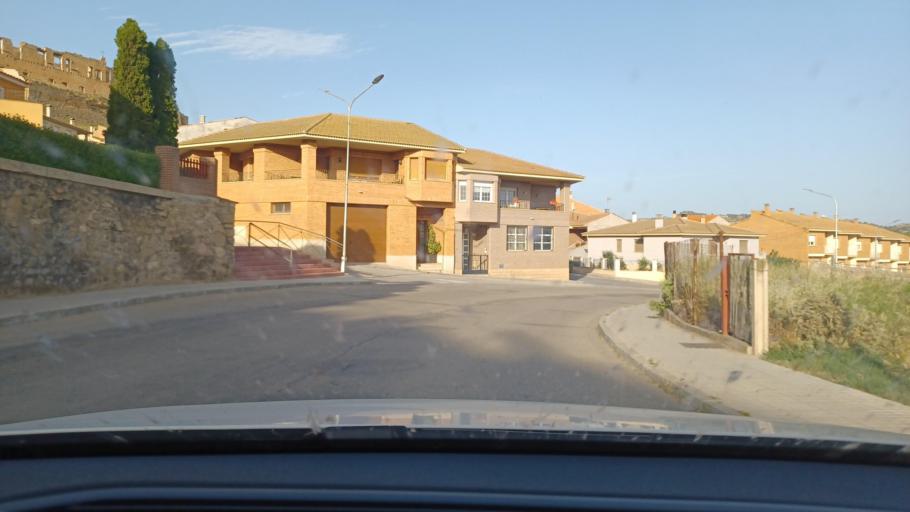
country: ES
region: Aragon
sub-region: Provincia de Zaragoza
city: Maella
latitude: 41.1210
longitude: 0.1399
